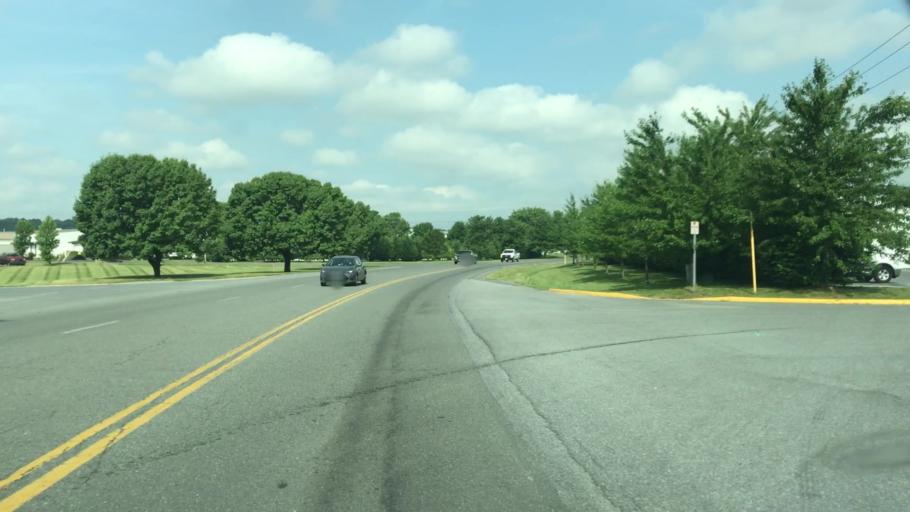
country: US
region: Virginia
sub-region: City of Winchester
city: Winchester
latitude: 39.2209
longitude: -78.1443
